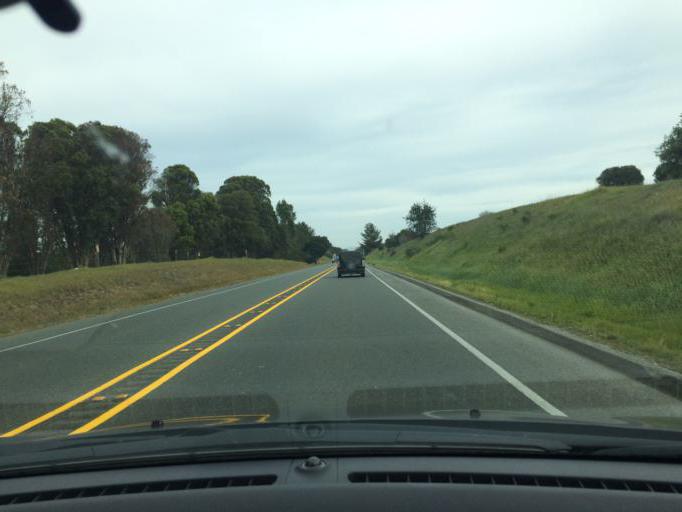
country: US
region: California
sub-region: Monterey County
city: Castroville
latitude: 36.7737
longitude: -121.7251
